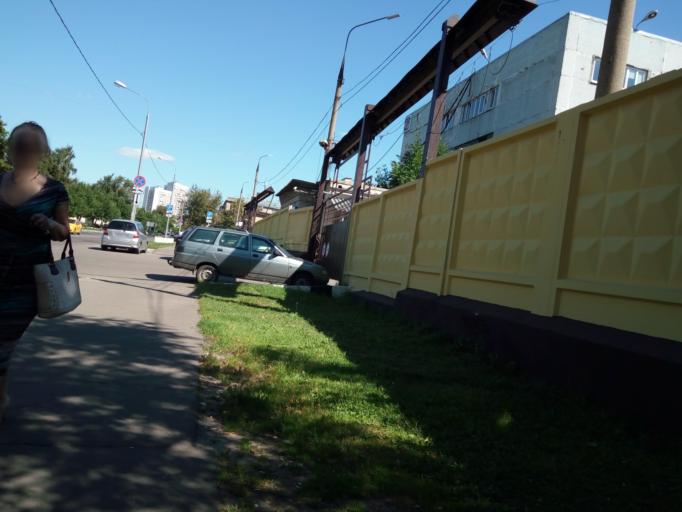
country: RU
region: Moscow
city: Sokol
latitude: 55.7722
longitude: 37.5184
